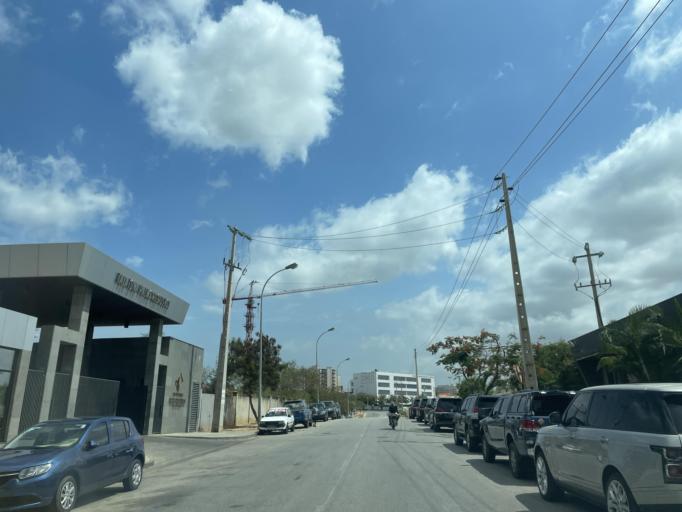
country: AO
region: Luanda
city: Luanda
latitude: -8.9261
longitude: 13.1932
